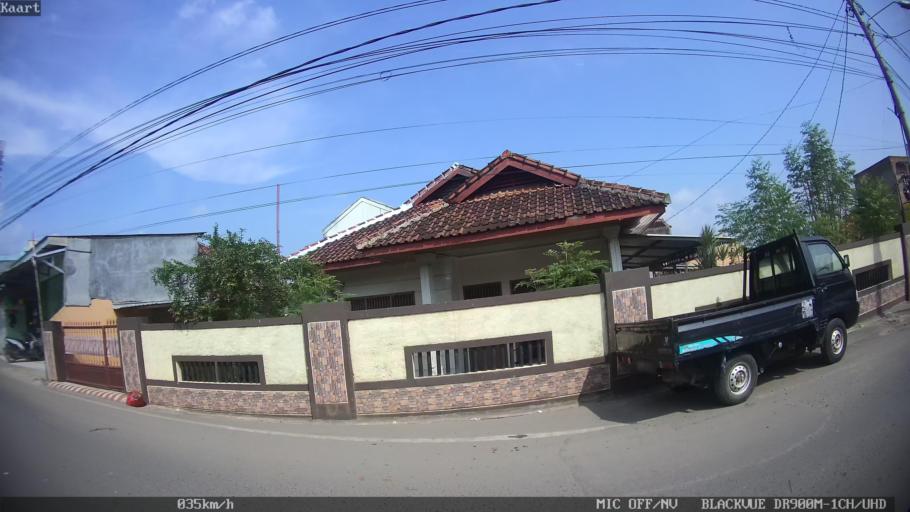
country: ID
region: Lampung
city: Kedaton
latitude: -5.3597
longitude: 105.2579
